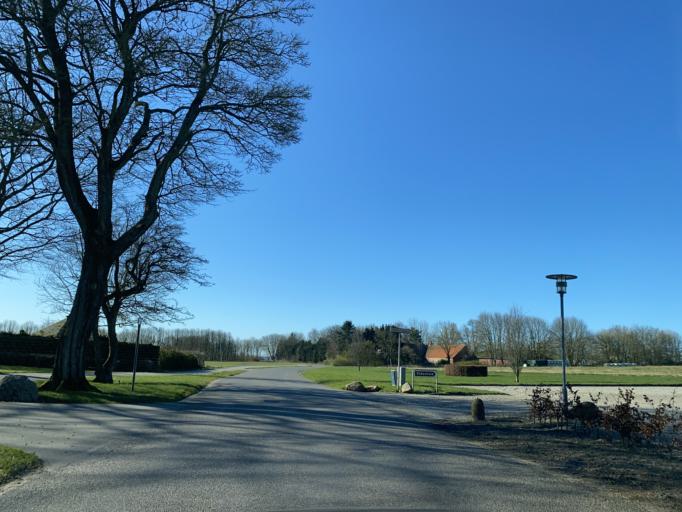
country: DK
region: Central Jutland
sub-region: Skanderborg Kommune
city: Skovby
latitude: 56.1940
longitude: 9.9650
